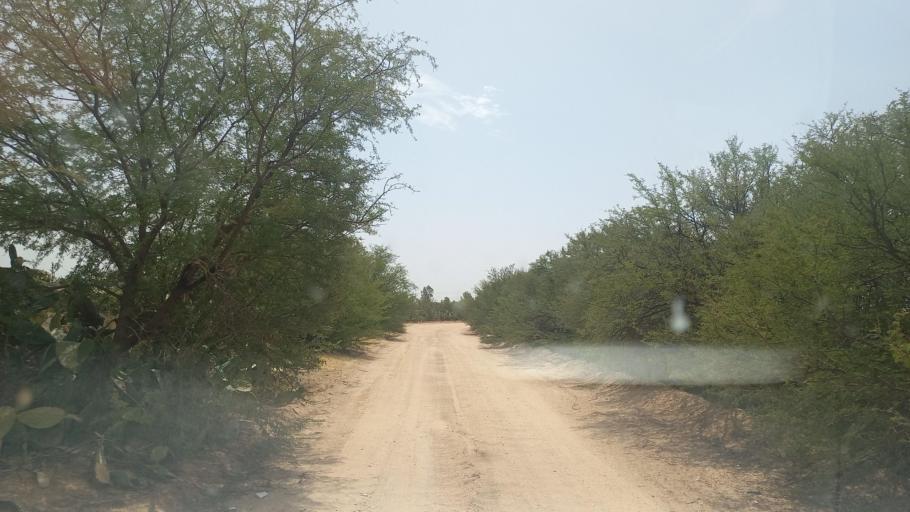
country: TN
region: Al Qasrayn
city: Kasserine
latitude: 35.2538
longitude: 9.0077
